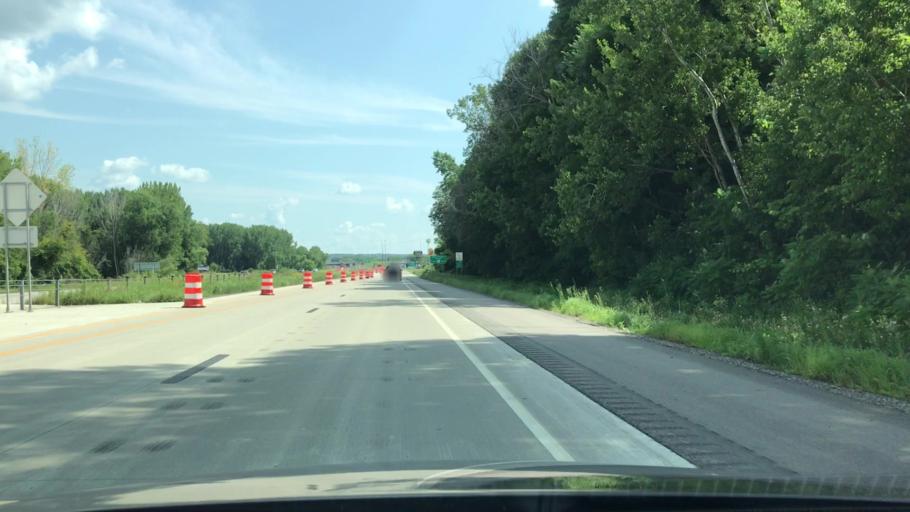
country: US
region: Minnesota
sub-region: Nicollet County
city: North Mankato
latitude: 44.2025
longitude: -94.0230
